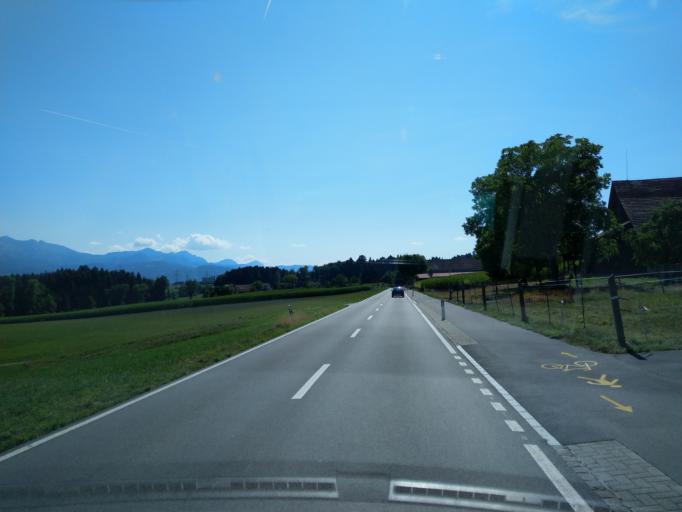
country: CH
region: Lucerne
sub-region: Hochdorf District
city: Ballwil
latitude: 47.1182
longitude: 8.2973
